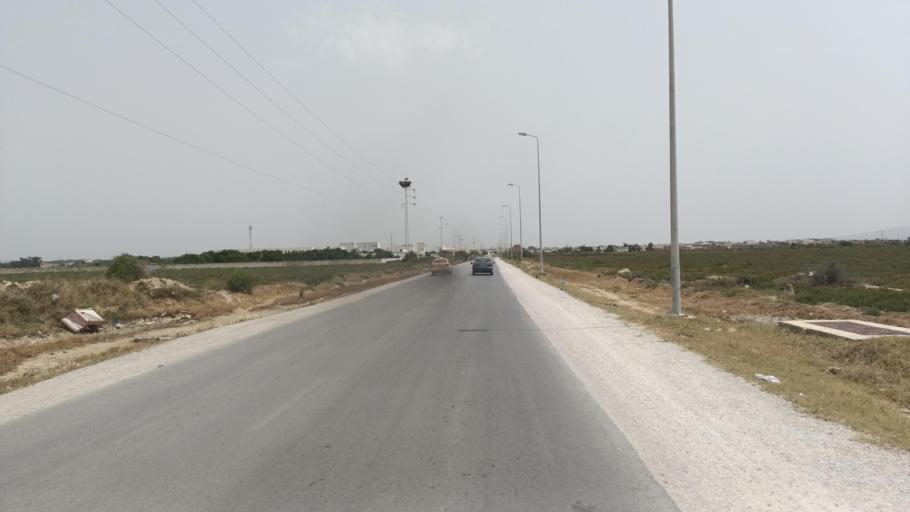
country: TN
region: Nabul
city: Manzil Bu Zalafah
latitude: 36.7154
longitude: 10.4787
